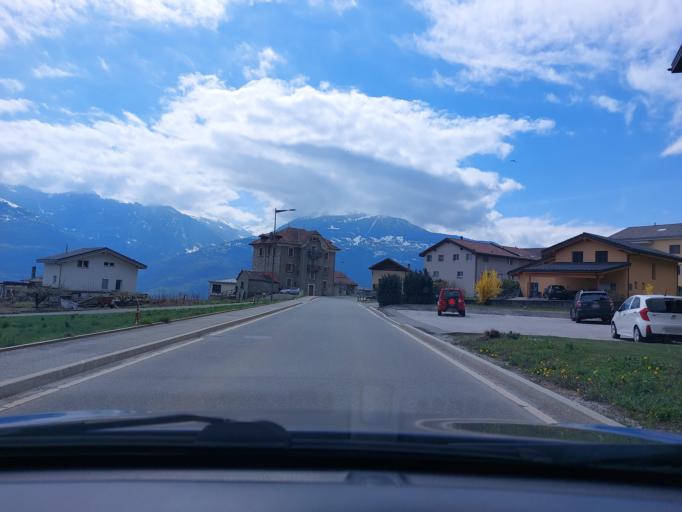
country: CH
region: Valais
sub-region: Conthey District
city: Conthey
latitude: 46.2418
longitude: 7.2958
